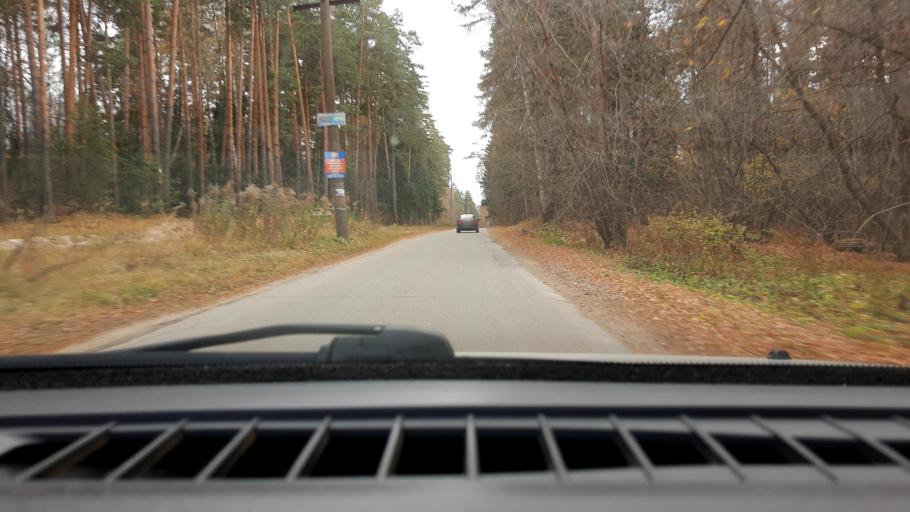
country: RU
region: Nizjnij Novgorod
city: Afonino
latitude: 56.1735
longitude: 44.0978
